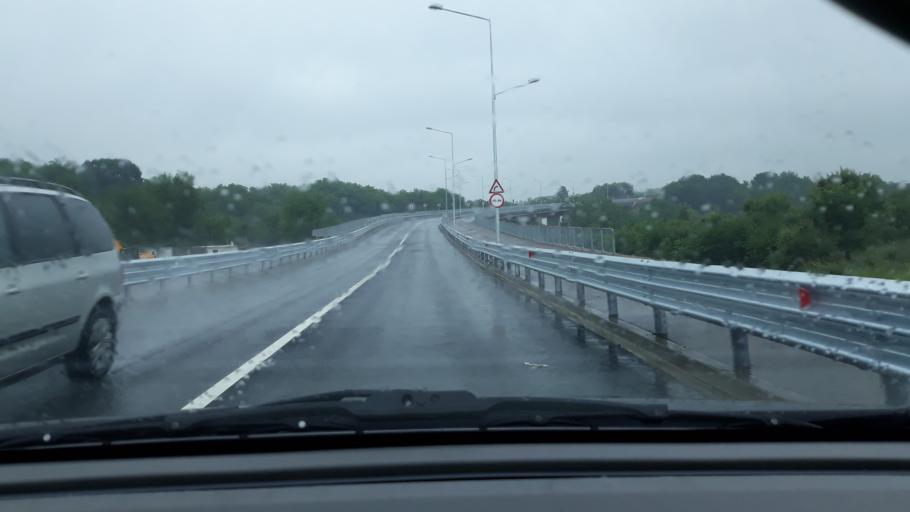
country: RO
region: Bihor
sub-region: Comuna Biharea
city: Biharea
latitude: 47.1121
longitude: 21.8998
